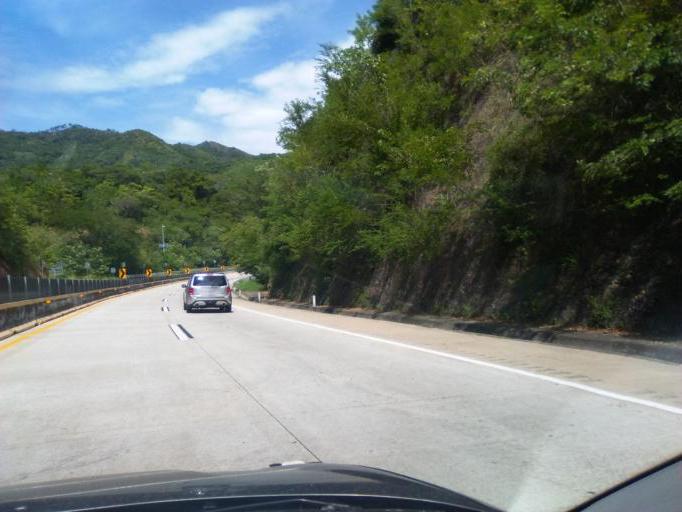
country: MX
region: Guerrero
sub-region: Acapulco de Juarez
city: Pueblo Madero (El Playon)
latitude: 17.0995
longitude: -99.5928
